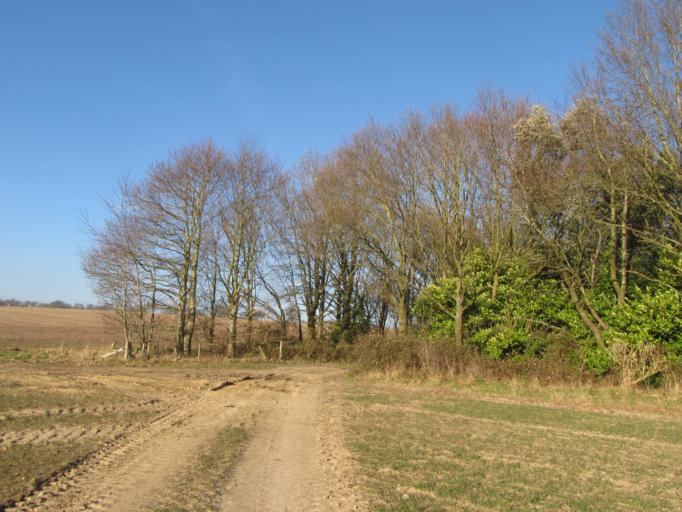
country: GB
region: England
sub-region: West Sussex
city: Petworth
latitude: 50.9780
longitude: -0.6309
